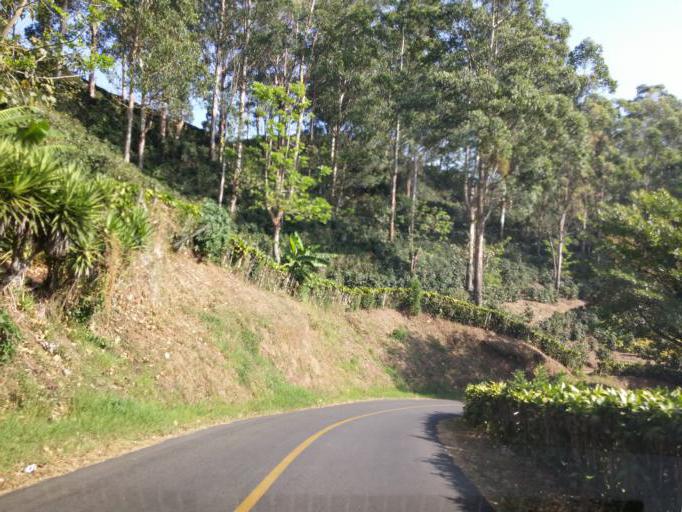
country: CR
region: Alajuela
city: Sabanilla
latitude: 10.0790
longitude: -84.1852
